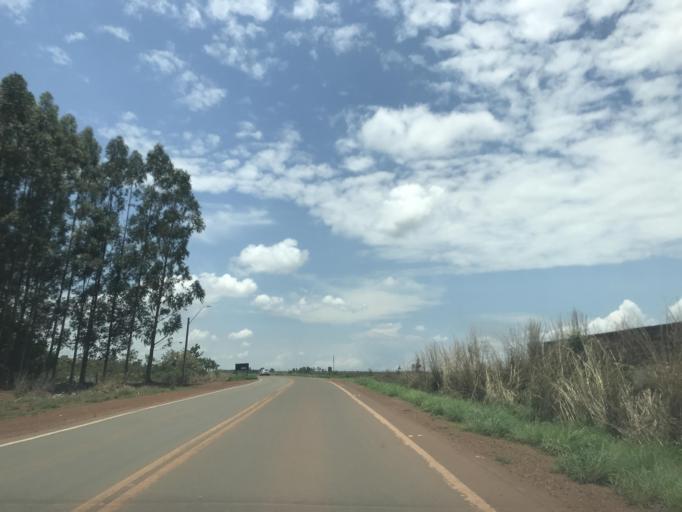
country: BR
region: Goias
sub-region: Luziania
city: Luziania
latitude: -16.4650
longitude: -48.2143
